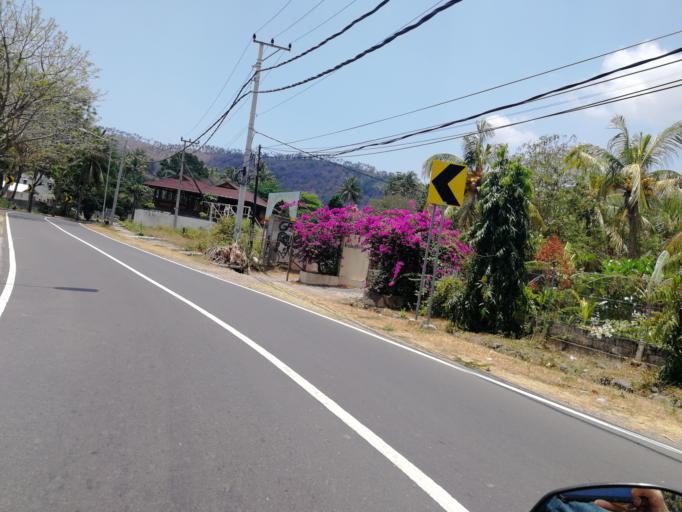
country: ID
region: West Nusa Tenggara
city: Karangsubagan
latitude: -8.4600
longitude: 116.0381
